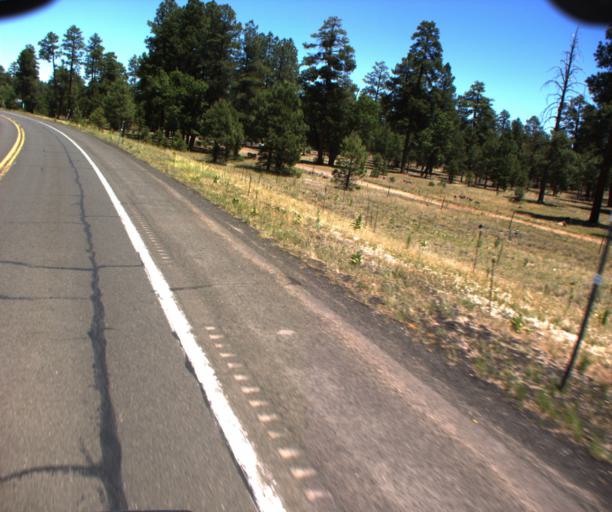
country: US
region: Arizona
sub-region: Gila County
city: Pine
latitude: 34.5533
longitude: -111.2898
